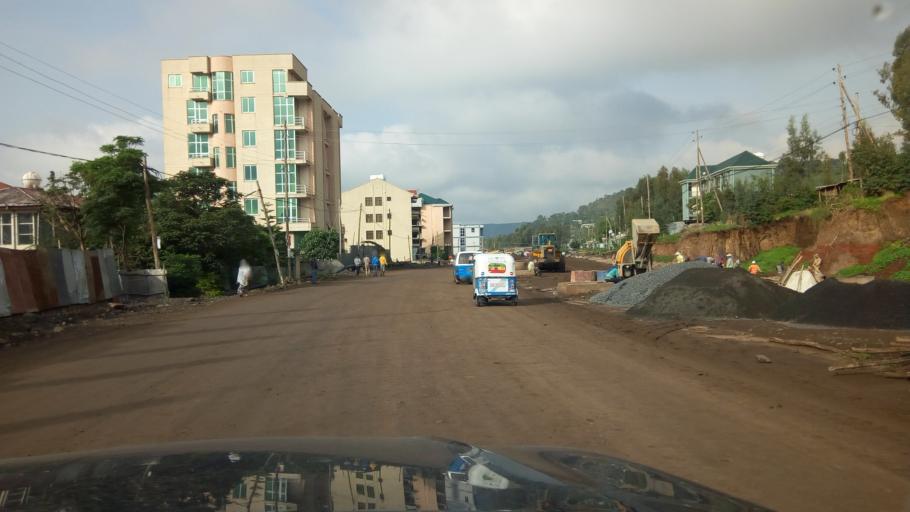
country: ET
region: Amhara
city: Gondar
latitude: 12.5667
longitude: 37.4342
